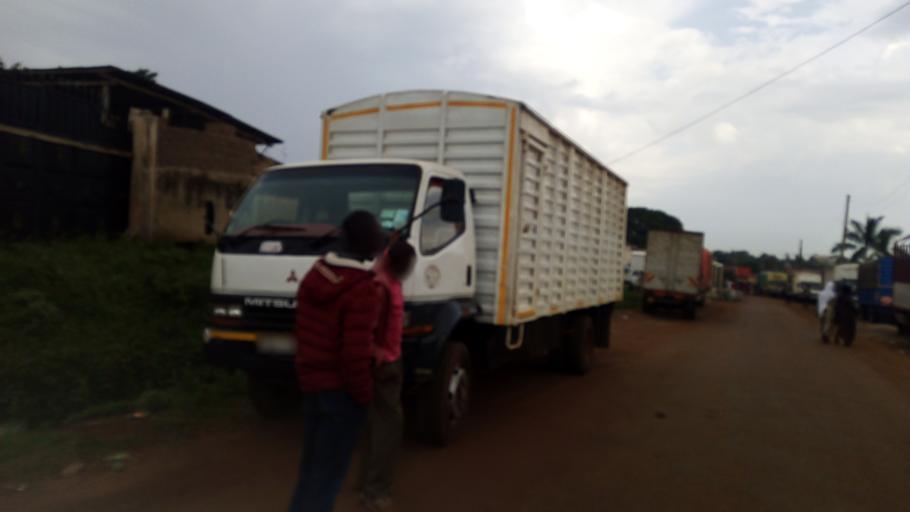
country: UG
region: Eastern Region
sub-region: Mbale District
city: Mbale
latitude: 1.0764
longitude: 34.1659
